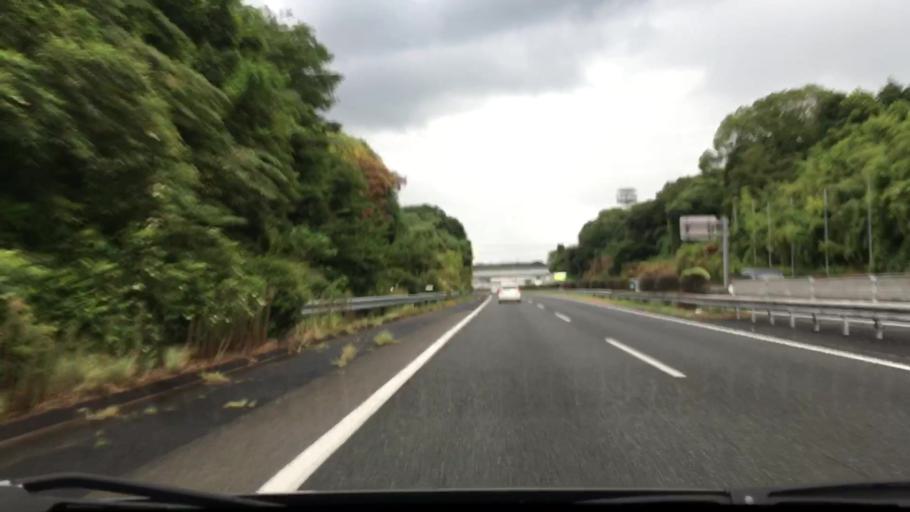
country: JP
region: Fukuoka
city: Miyata
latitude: 33.7463
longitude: 130.6164
